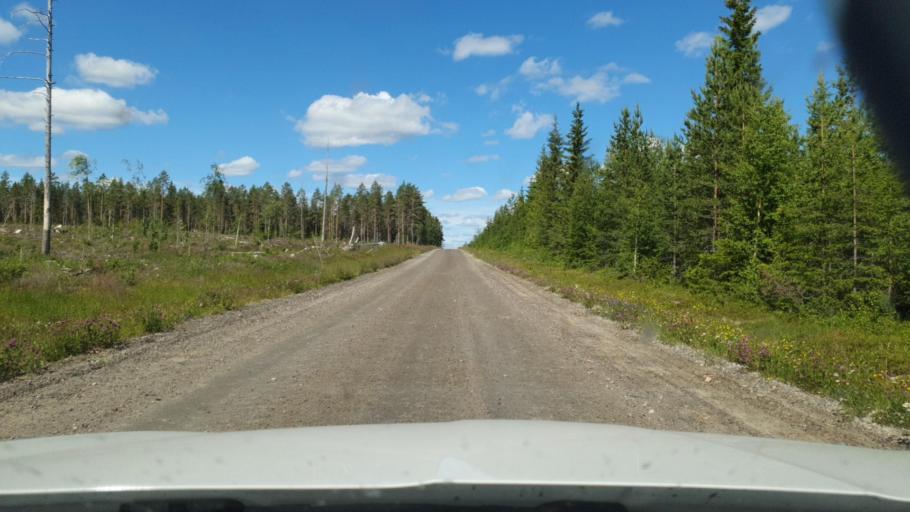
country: SE
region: Vaesterbotten
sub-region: Skelleftea Kommun
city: Byske
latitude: 65.1314
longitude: 21.1968
